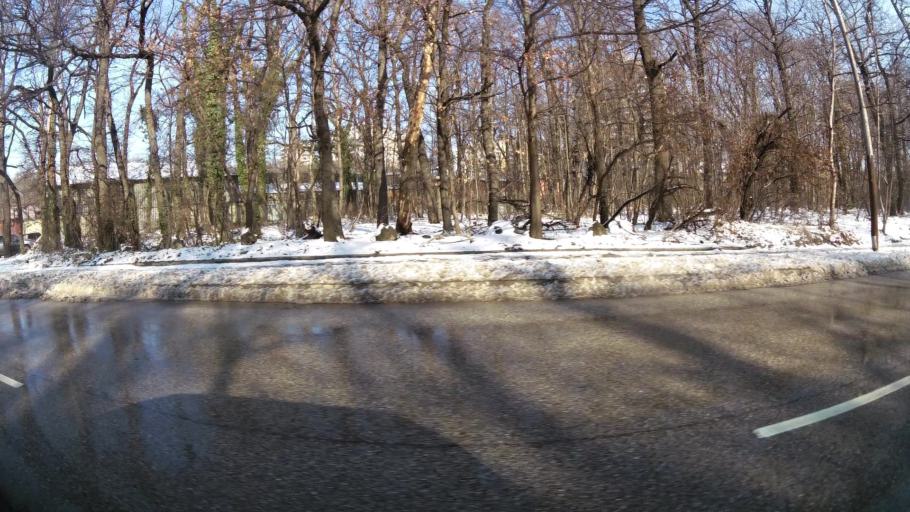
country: BG
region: Sofia-Capital
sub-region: Stolichna Obshtina
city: Sofia
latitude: 42.6664
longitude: 23.3420
